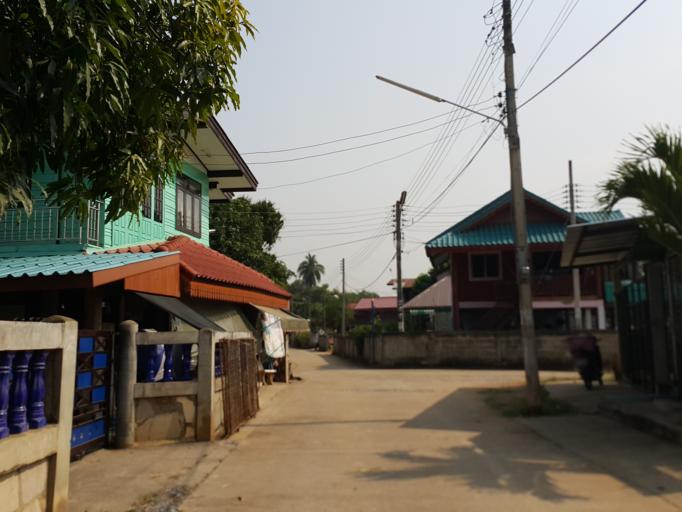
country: TH
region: Sukhothai
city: Thung Saliam
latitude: 17.3250
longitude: 99.5205
